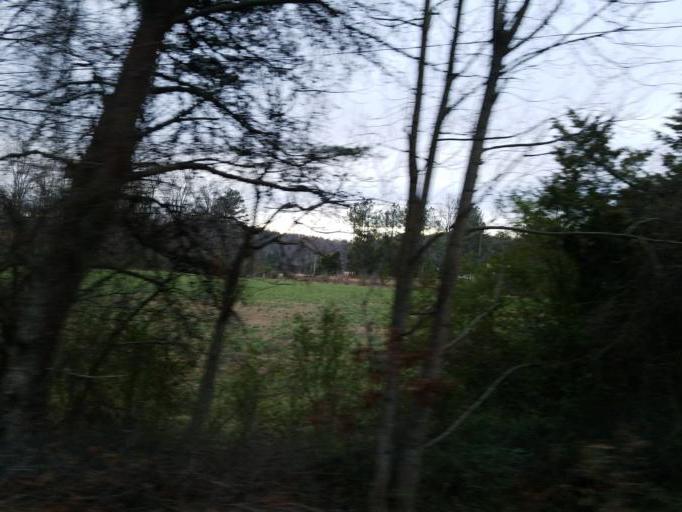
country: US
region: Georgia
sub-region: Dawson County
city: Dawsonville
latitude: 34.4171
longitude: -84.0310
